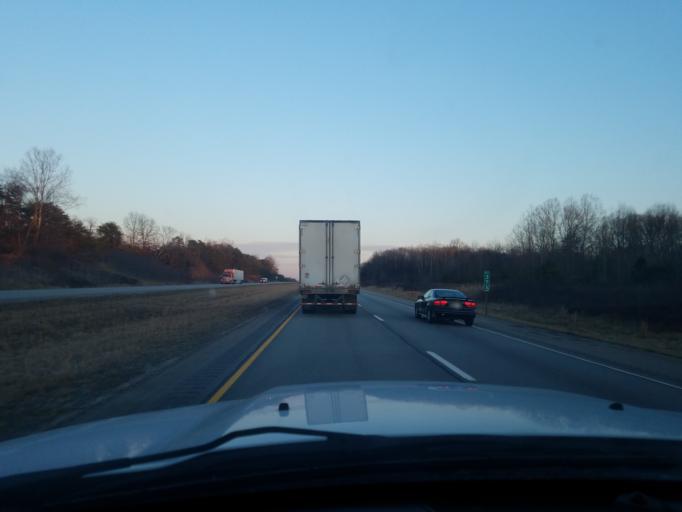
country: US
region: Indiana
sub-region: Gibson County
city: Oakland City
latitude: 38.1923
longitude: -87.3278
